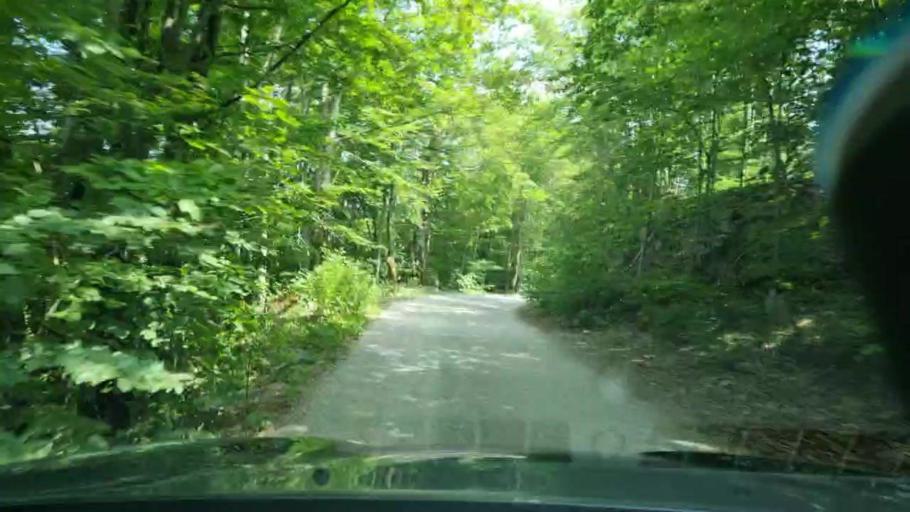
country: BA
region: Federation of Bosnia and Herzegovina
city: Bosansko Grahovo
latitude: 44.2990
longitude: 16.2664
